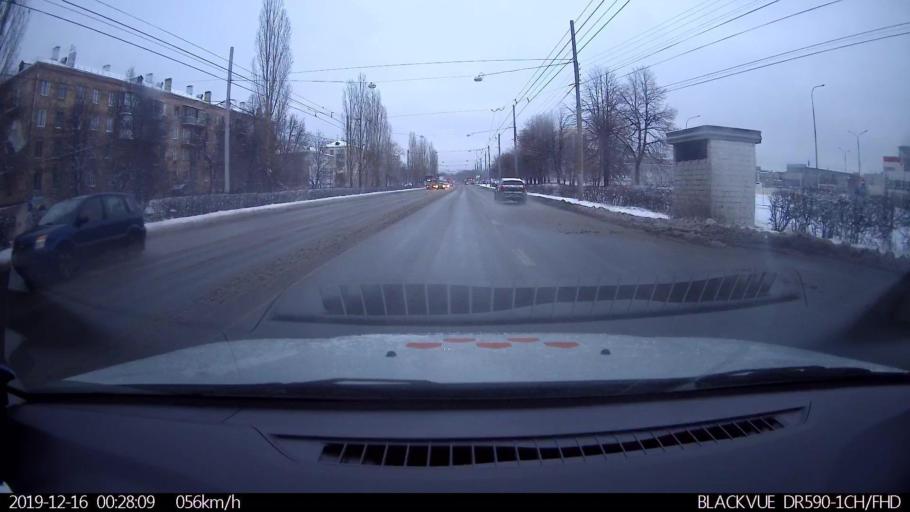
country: RU
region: Nizjnij Novgorod
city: Nizhniy Novgorod
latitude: 56.3275
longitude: 43.9082
